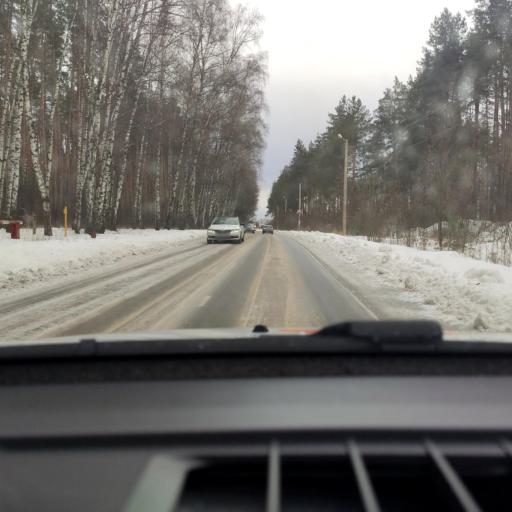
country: RU
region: Voronezj
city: Podgornoye
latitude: 51.7506
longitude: 39.1573
